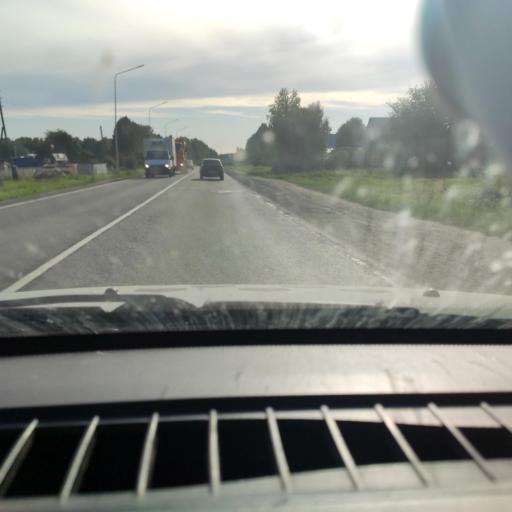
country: RU
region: Kirov
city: Vakhrushi
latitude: 58.6583
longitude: 49.9152
